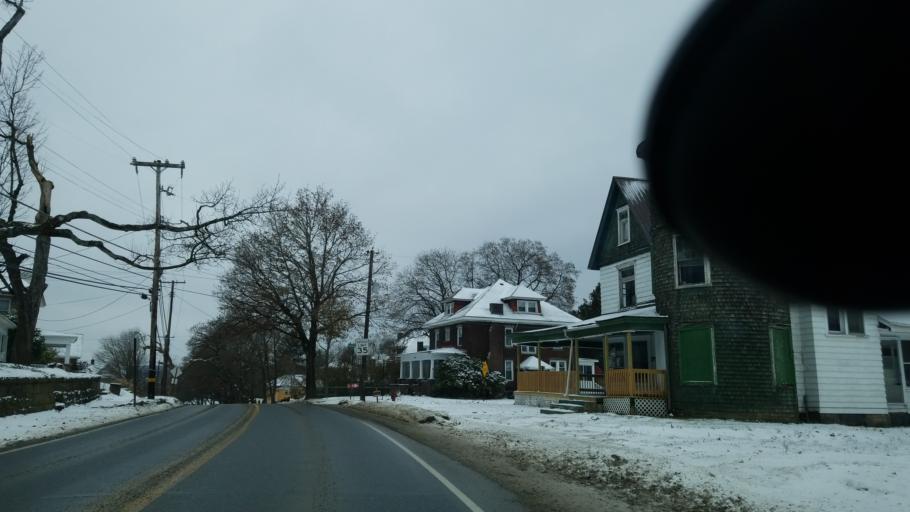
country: US
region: Pennsylvania
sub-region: Jefferson County
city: Punxsutawney
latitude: 40.9437
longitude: -78.9569
